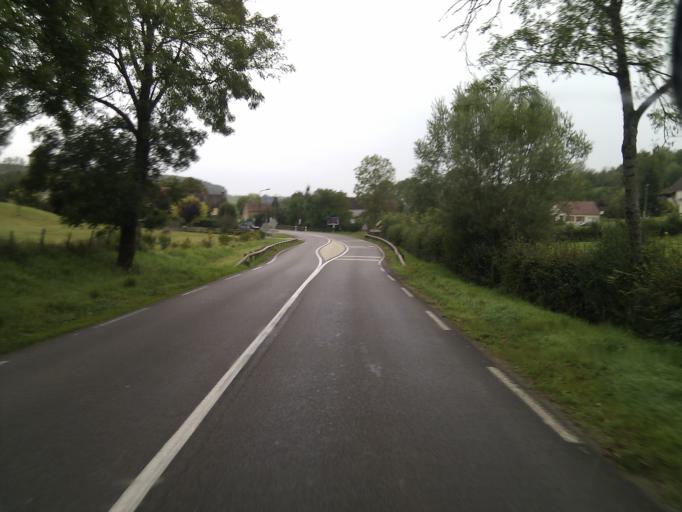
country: FR
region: Bourgogne
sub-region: Departement de la Cote-d'Or
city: Montbard
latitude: 47.5532
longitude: 4.3483
